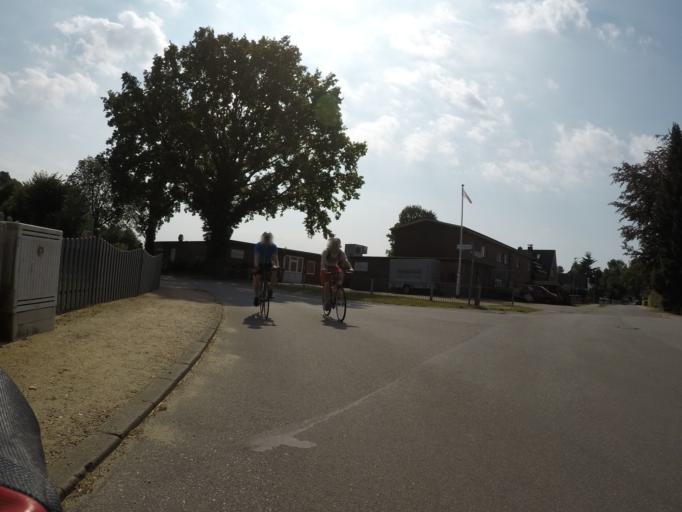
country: DE
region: Hamburg
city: Lemsahl-Mellingstedt
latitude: 53.6980
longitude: 10.0481
